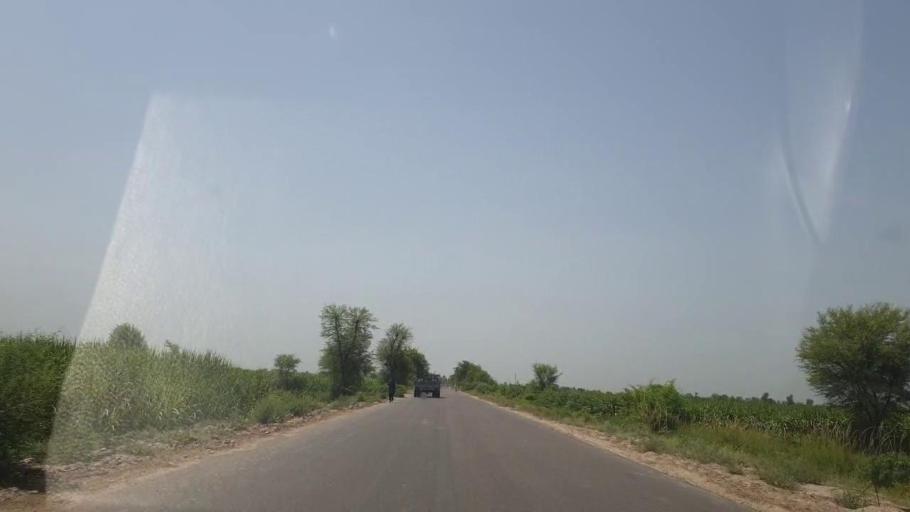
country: PK
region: Sindh
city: Gambat
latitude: 27.2979
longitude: 68.6052
